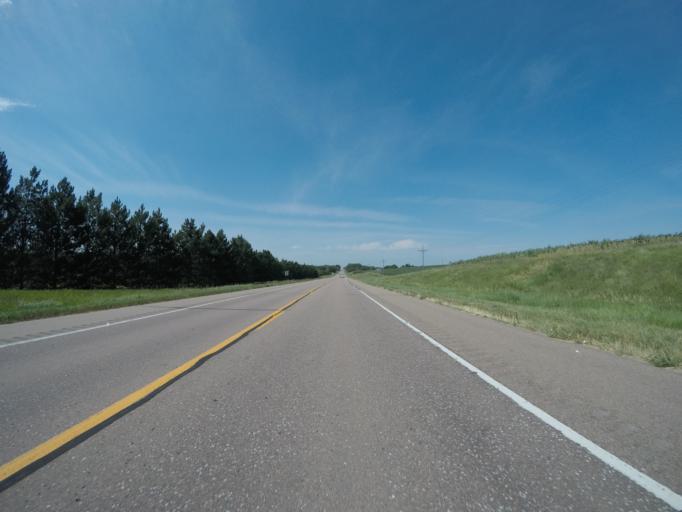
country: US
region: Nebraska
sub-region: Webster County
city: Red Cloud
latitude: 40.3217
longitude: -98.4440
